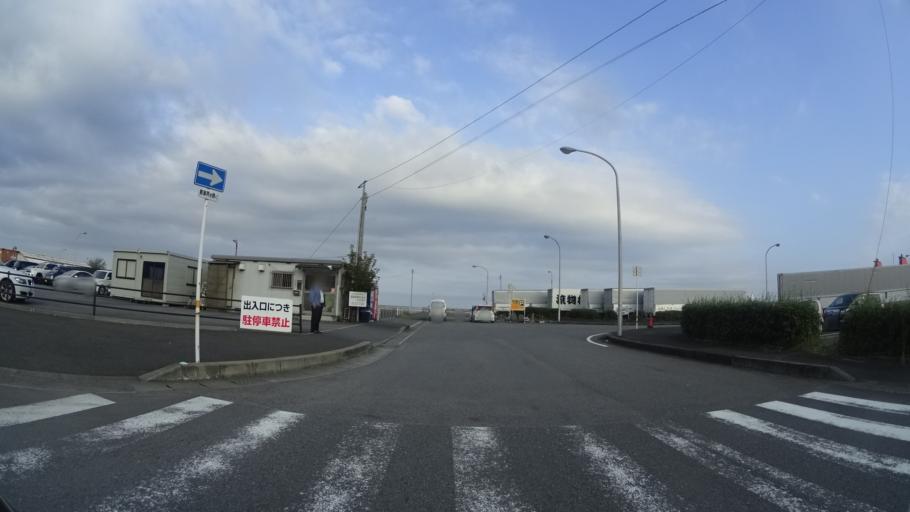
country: JP
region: Oita
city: Beppu
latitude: 33.3056
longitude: 131.5030
